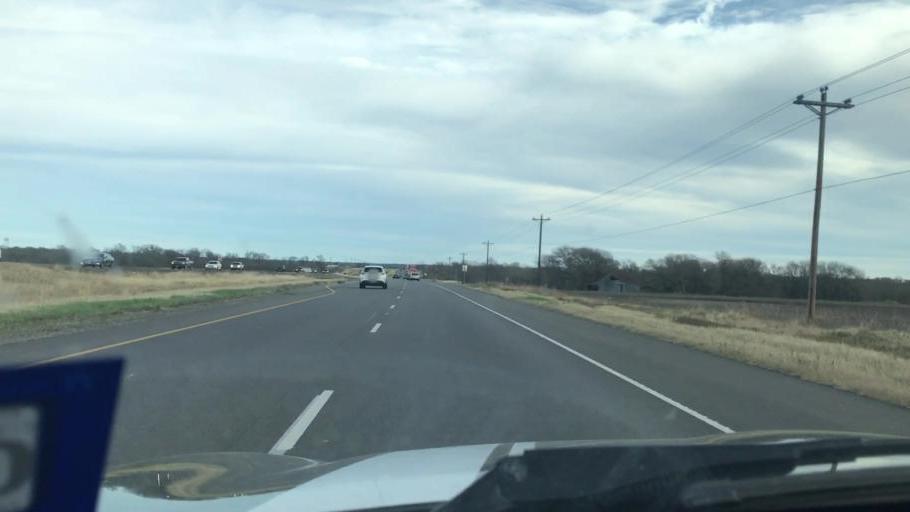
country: US
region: Texas
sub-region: Bastrop County
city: Elgin
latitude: 30.3513
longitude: -97.4441
